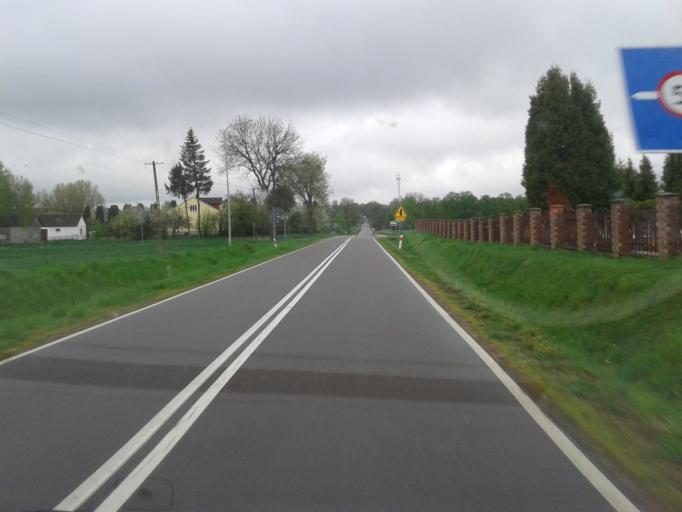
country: PL
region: Lublin Voivodeship
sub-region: Powiat tomaszowski
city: Telatyn
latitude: 50.5283
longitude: 23.9162
